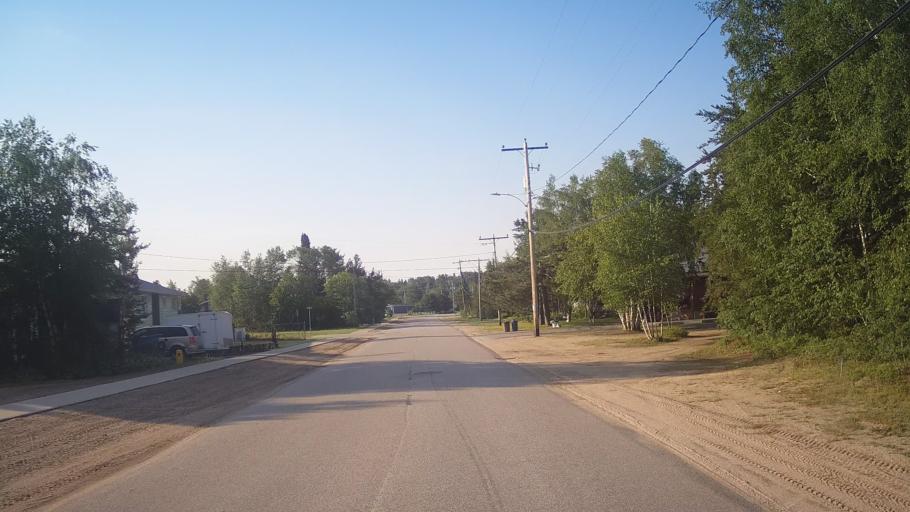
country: CA
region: Ontario
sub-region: Rainy River District
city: Atikokan
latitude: 49.4083
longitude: -91.6578
